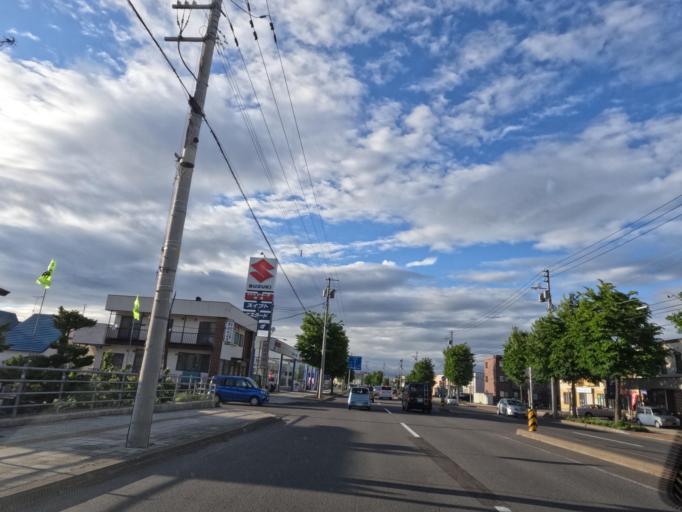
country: JP
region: Hokkaido
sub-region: Asahikawa-shi
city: Asahikawa
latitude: 43.7459
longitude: 142.3578
